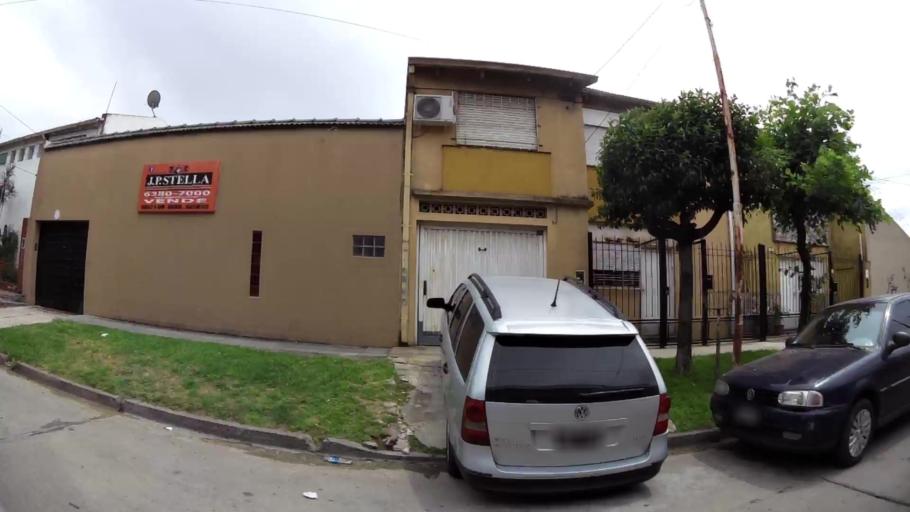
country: AR
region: Buenos Aires
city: San Justo
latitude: -34.6682
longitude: -58.5204
